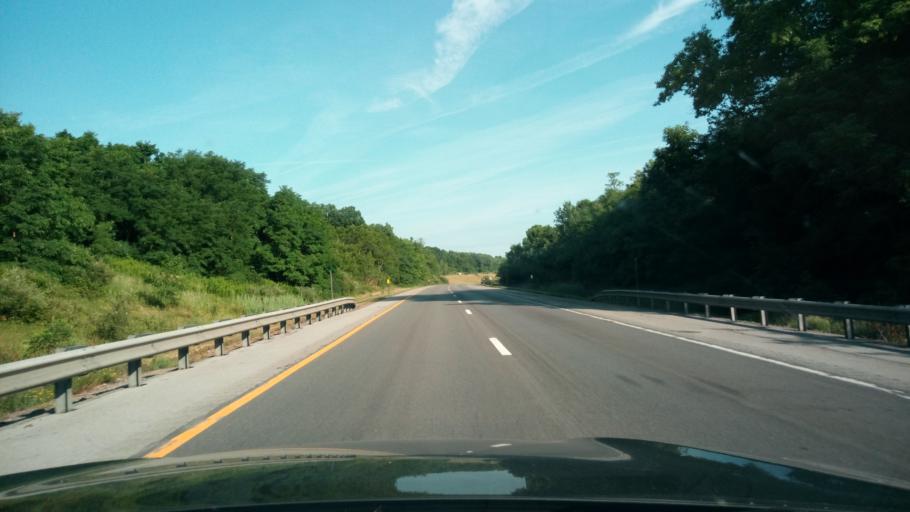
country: US
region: New York
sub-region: Livingston County
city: Dansville
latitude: 42.6091
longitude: -77.7615
